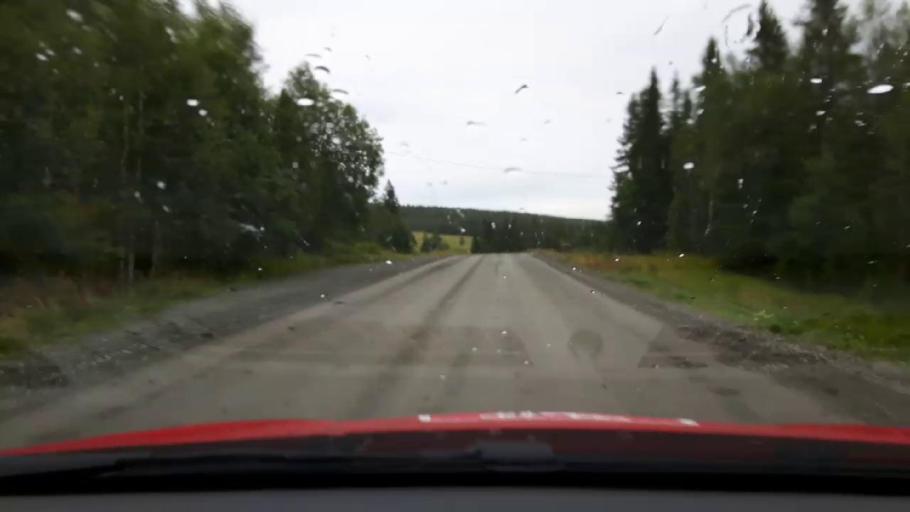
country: SE
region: Jaemtland
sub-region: Are Kommun
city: Are
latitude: 63.4636
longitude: 12.6245
